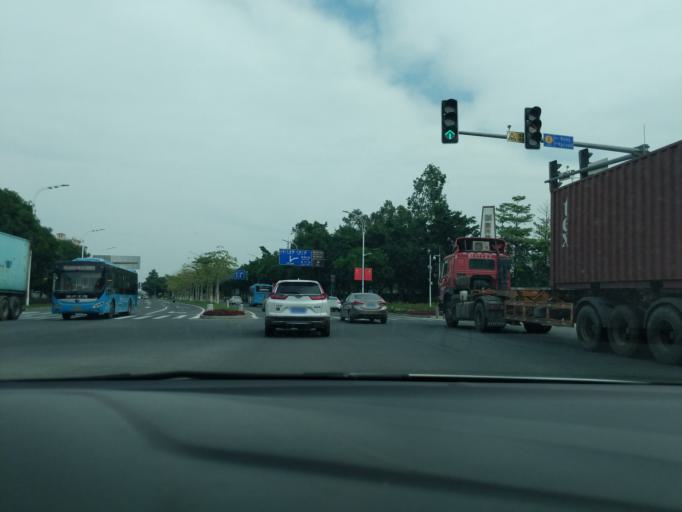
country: CN
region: Guangdong
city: Nansha
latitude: 22.7513
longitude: 113.5789
